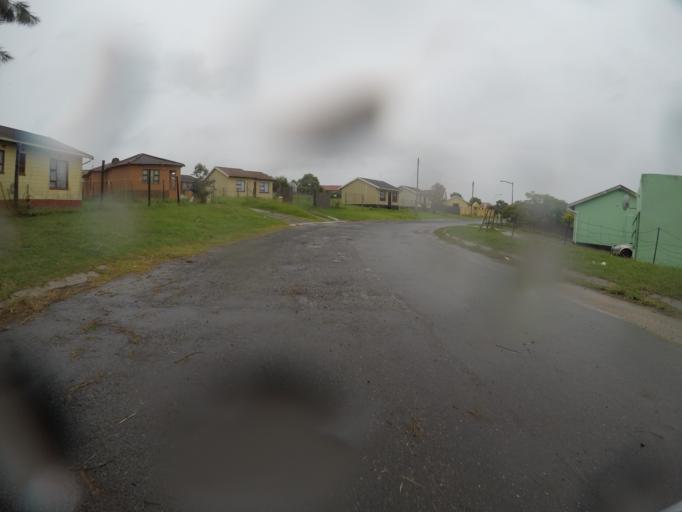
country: ZA
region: Eastern Cape
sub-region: Buffalo City Metropolitan Municipality
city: East London
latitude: -32.9927
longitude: 27.8384
